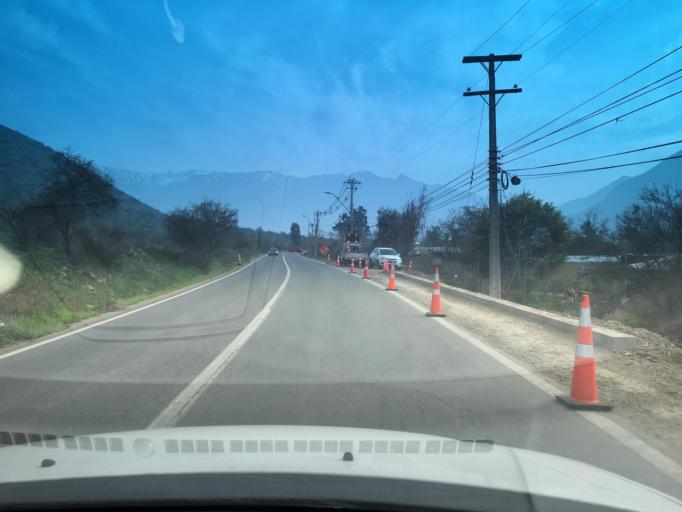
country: CL
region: Santiago Metropolitan
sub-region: Provincia de Chacabuco
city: Lampa
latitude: -33.2645
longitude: -70.8966
